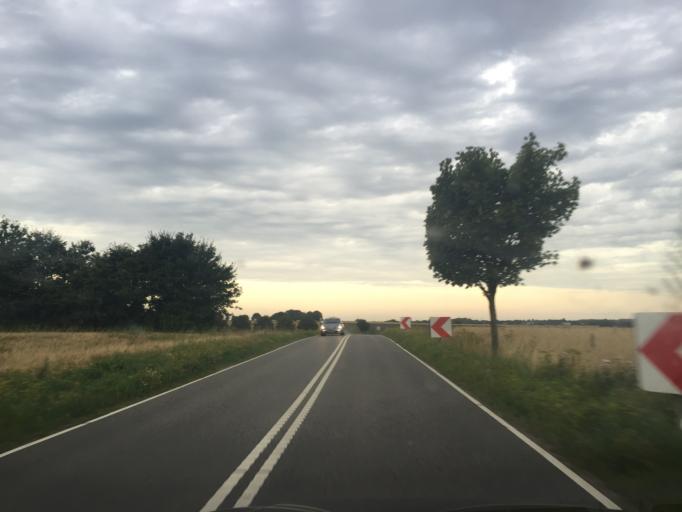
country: DK
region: Capital Region
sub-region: Egedal Kommune
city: Stenlose
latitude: 55.7337
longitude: 12.1895
